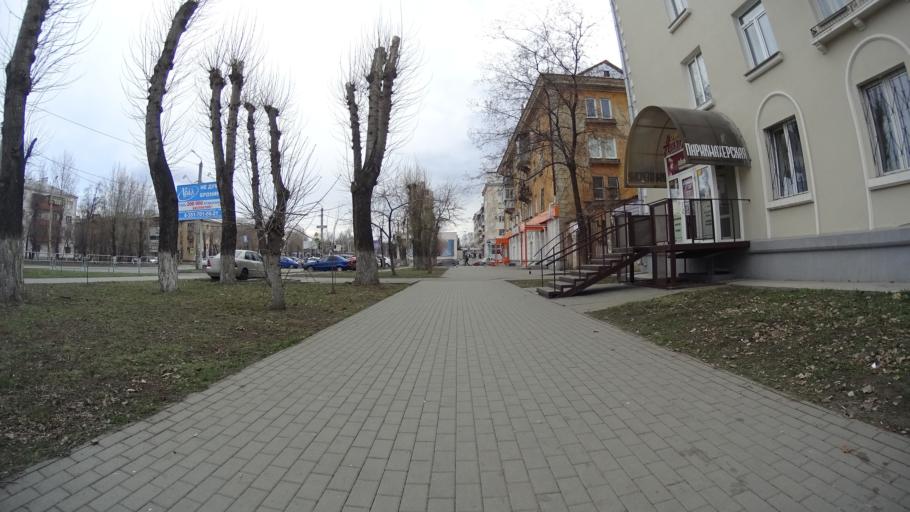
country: RU
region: Chelyabinsk
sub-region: Gorod Chelyabinsk
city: Chelyabinsk
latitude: 55.1628
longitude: 61.4412
